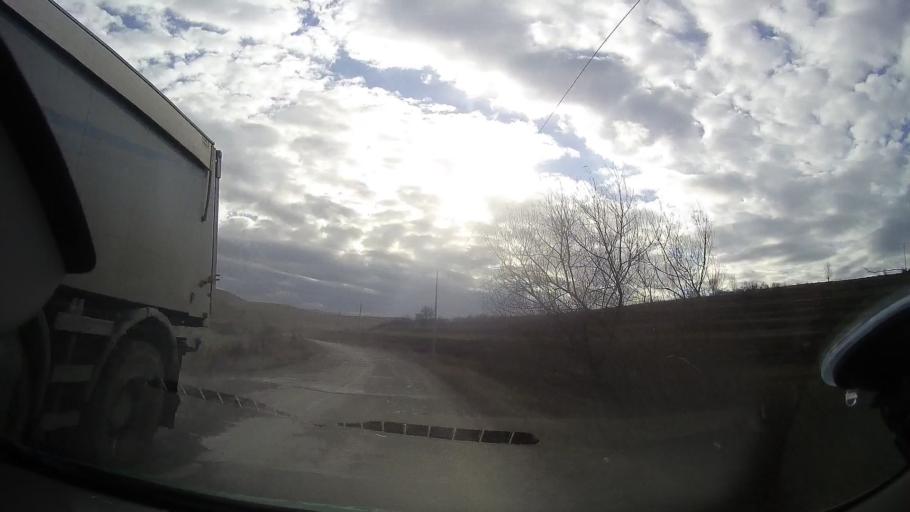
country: RO
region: Cluj
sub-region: Comuna Baisoara
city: Baisoara
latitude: 46.6050
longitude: 23.4595
